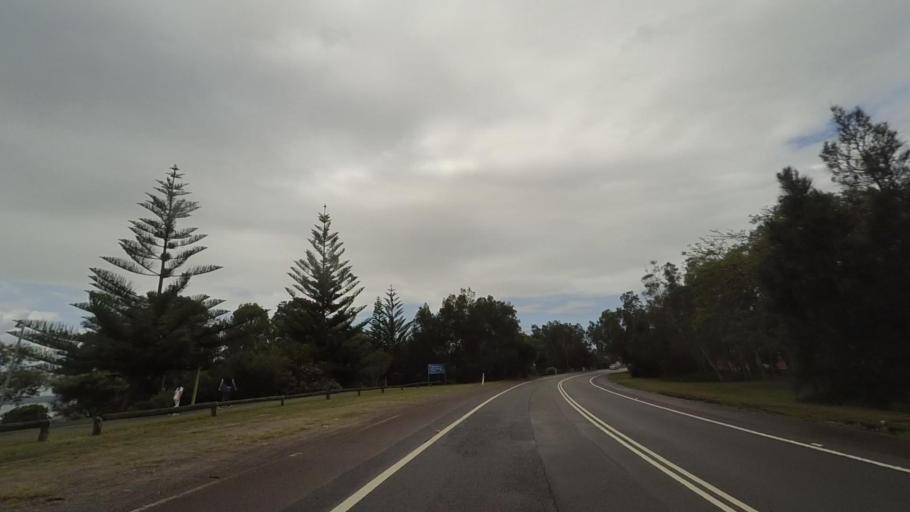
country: AU
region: New South Wales
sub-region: Wyong Shire
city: The Entrance
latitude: -33.3283
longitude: 151.5026
